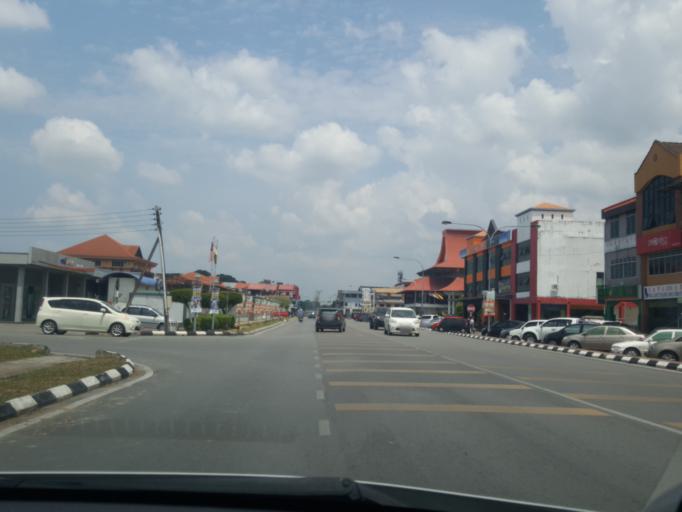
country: MY
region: Sarawak
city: Sarikei
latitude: 2.1322
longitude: 111.5241
